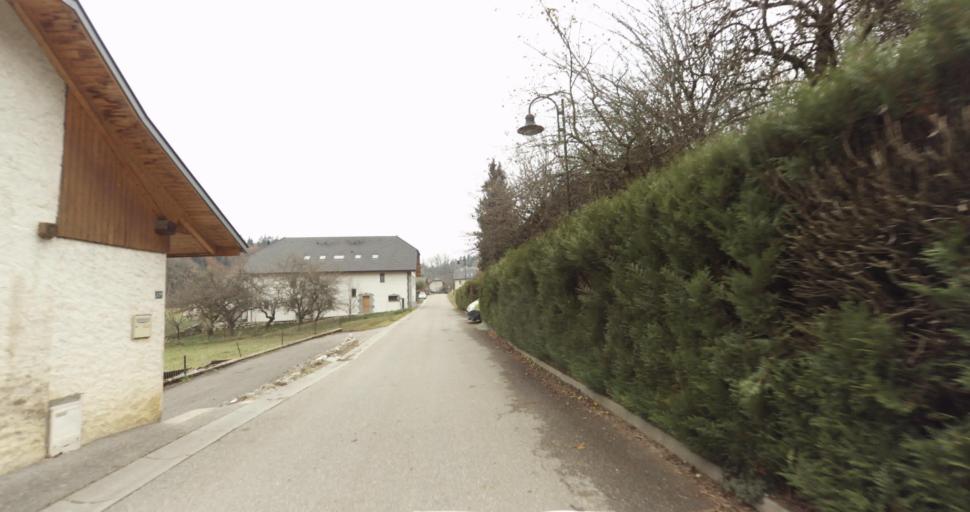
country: FR
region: Rhone-Alpes
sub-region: Departement de la Haute-Savoie
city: Doussard
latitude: 45.7925
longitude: 6.1895
